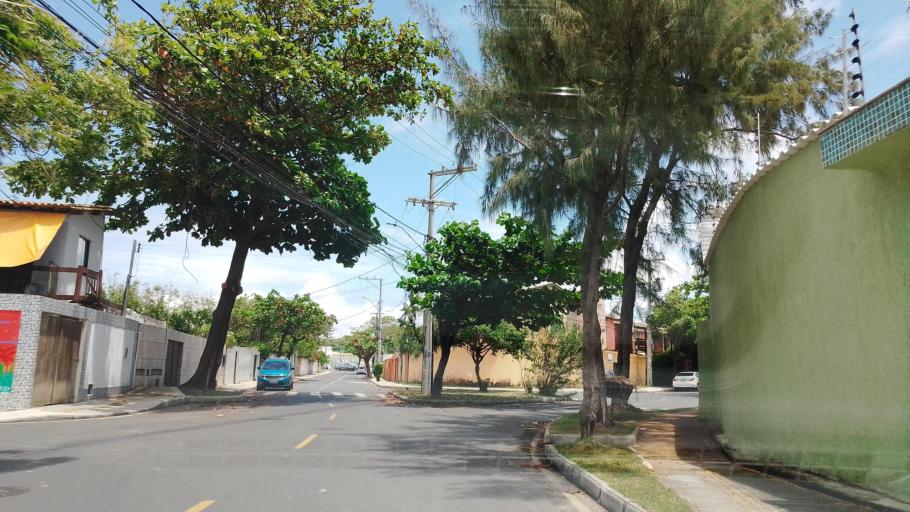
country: BR
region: Bahia
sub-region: Lauro De Freitas
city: Lauro de Freitas
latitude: -12.9344
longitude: -38.3284
